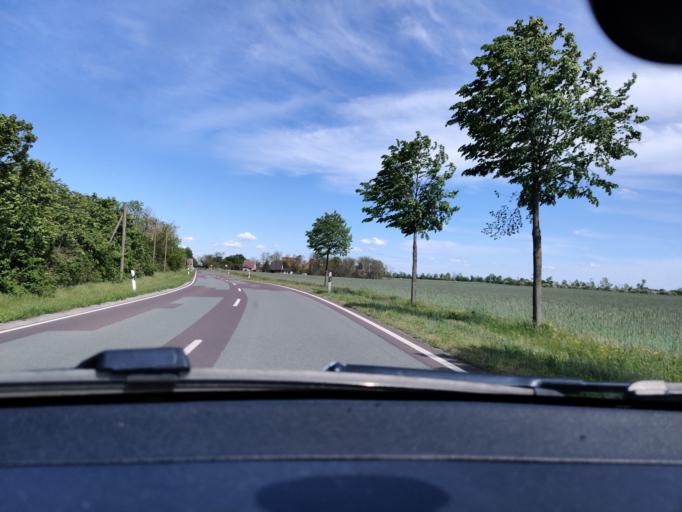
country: DE
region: Saxony-Anhalt
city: Mockern
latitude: 52.1198
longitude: 11.9298
